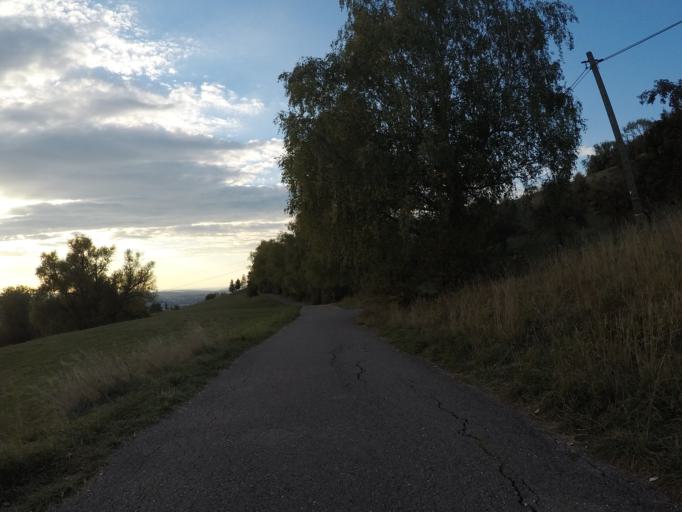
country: DE
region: Baden-Wuerttemberg
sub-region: Tuebingen Region
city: Eningen unter Achalm
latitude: 48.4899
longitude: 9.2438
